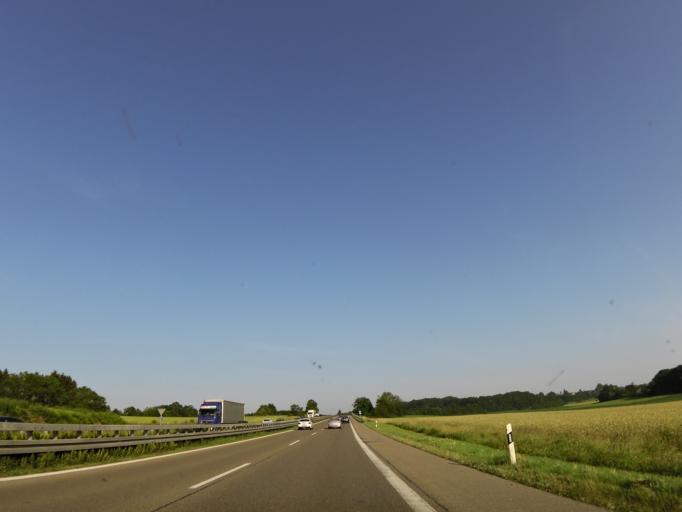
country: DE
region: Baden-Wuerttemberg
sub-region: Regierungsbezirk Stuttgart
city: Hohenstadt
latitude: 48.5315
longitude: 9.6768
